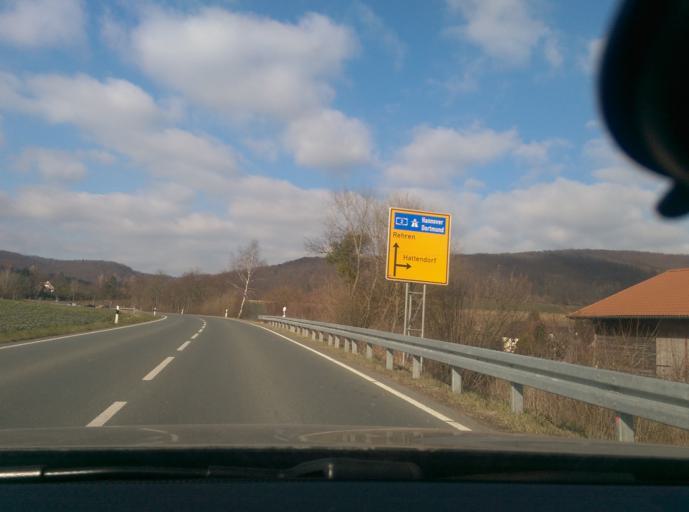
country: DE
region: Lower Saxony
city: Hessisch Oldendorf
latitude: 52.1892
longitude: 9.2502
